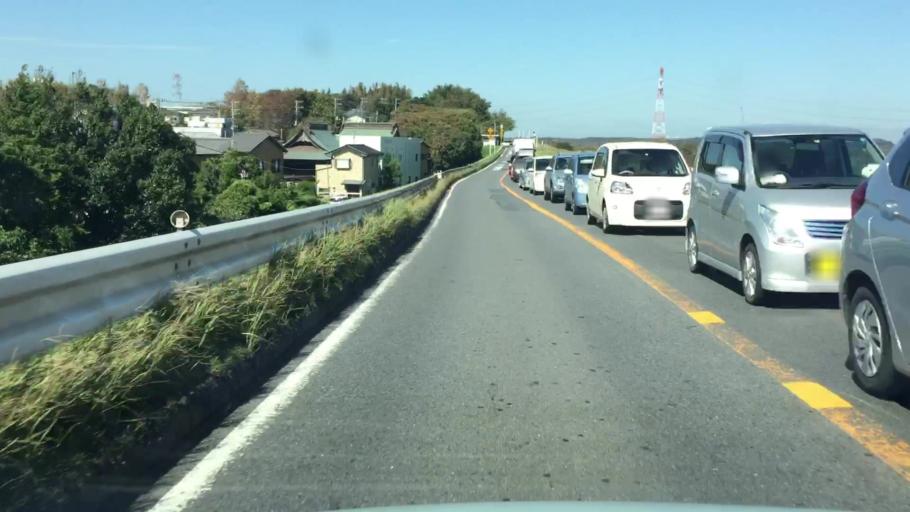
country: JP
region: Ibaraki
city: Ryugasaki
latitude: 35.8547
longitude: 140.1366
